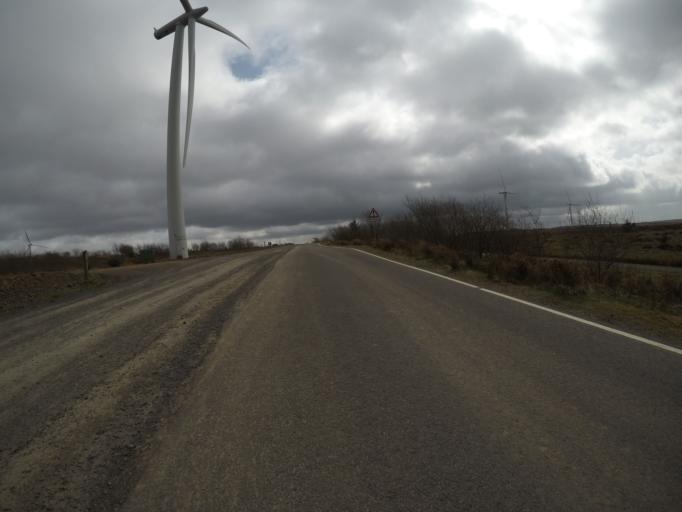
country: GB
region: Scotland
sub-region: East Renfrewshire
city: Newton Mearns
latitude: 55.7010
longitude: -4.3521
